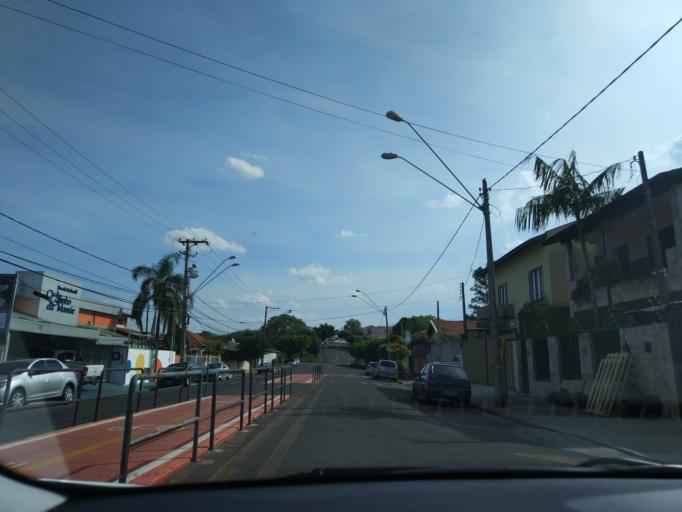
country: BR
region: Sao Paulo
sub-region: Botucatu
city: Botucatu
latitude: -22.8667
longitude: -48.4403
